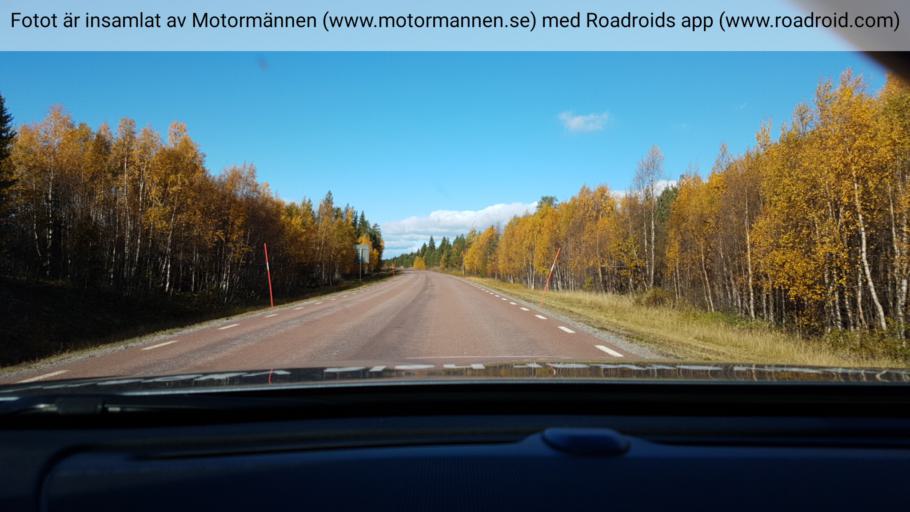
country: SE
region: Norrbotten
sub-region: Arjeplogs Kommun
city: Arjeplog
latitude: 65.9911
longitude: 18.1809
